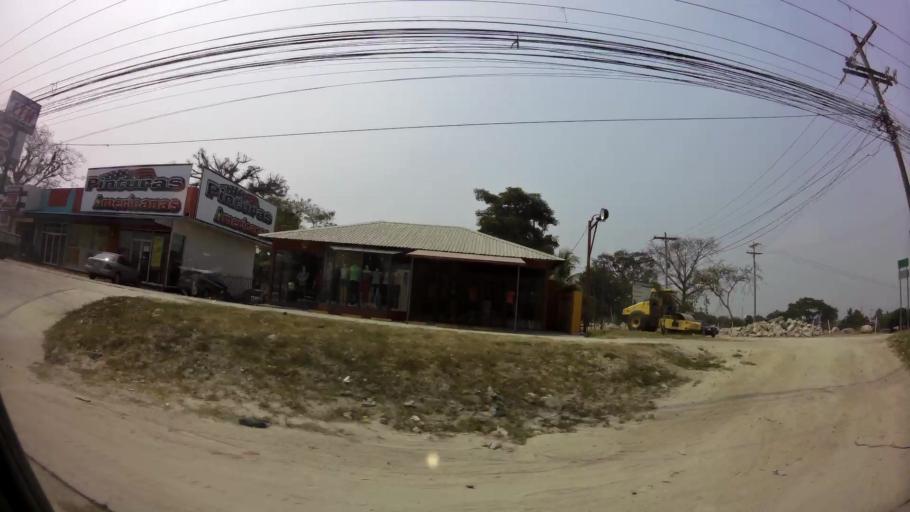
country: HN
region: Cortes
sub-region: San Pedro Sula
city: Pena Blanca
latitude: 15.5487
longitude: -88.0078
